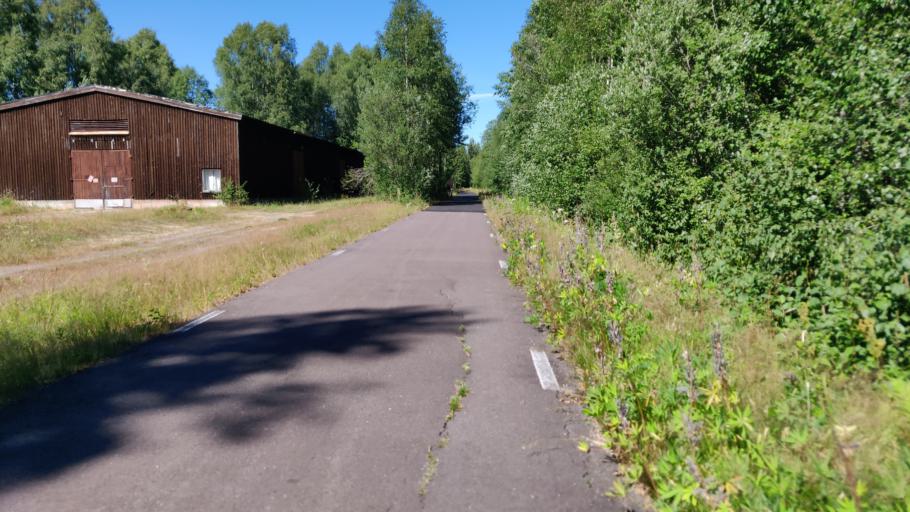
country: SE
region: Vaermland
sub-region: Hagfors Kommun
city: Hagfors
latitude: 59.9667
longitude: 13.5721
